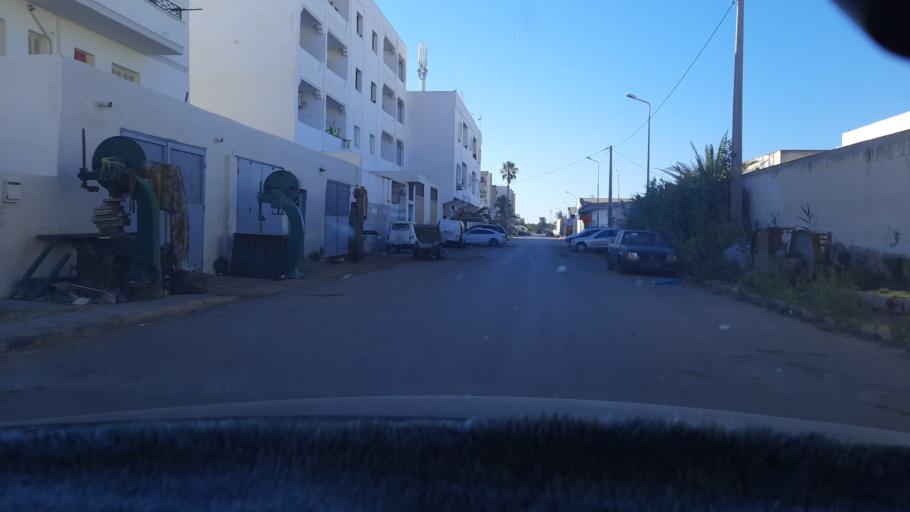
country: TN
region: Safaqis
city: Sfax
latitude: 34.7309
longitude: 10.7486
